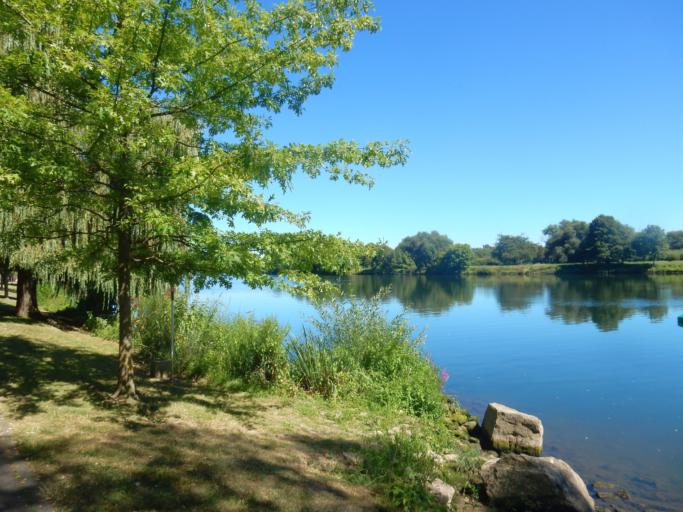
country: LU
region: Grevenmacher
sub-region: Canton de Remich
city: Remich
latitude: 49.5305
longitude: 6.3557
